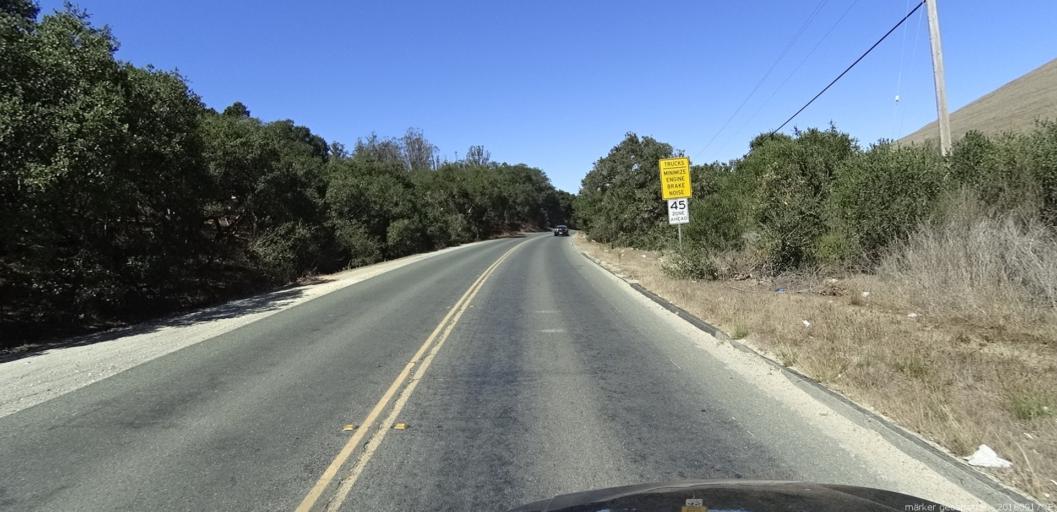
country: US
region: California
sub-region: Monterey County
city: Prunedale
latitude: 36.8093
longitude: -121.6237
